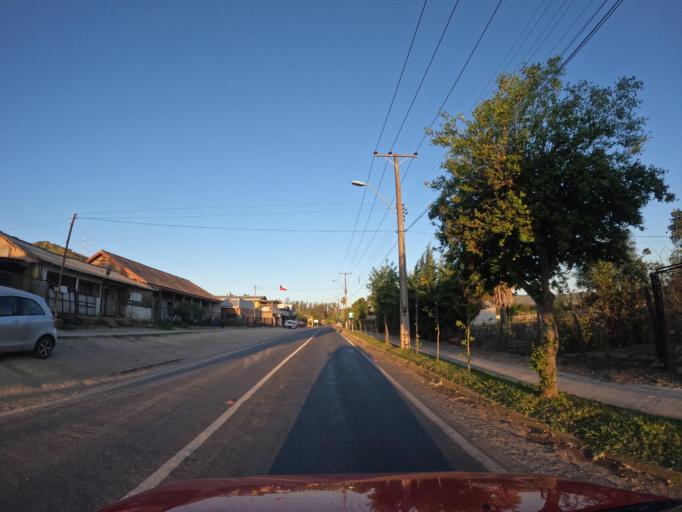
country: CL
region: Maule
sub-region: Provincia de Talca
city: Talca
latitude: -35.0899
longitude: -71.6535
